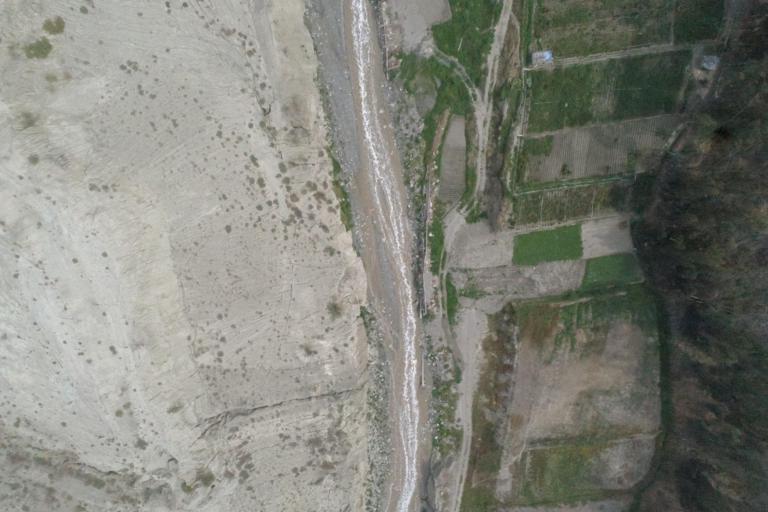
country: BO
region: La Paz
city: La Paz
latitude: -16.5977
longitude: -68.0665
